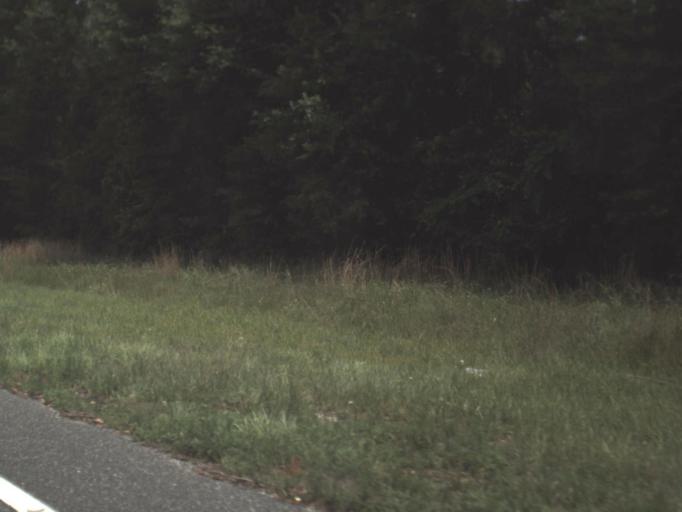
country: US
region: Florida
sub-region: Taylor County
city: Perry
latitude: 29.9720
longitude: -83.4809
